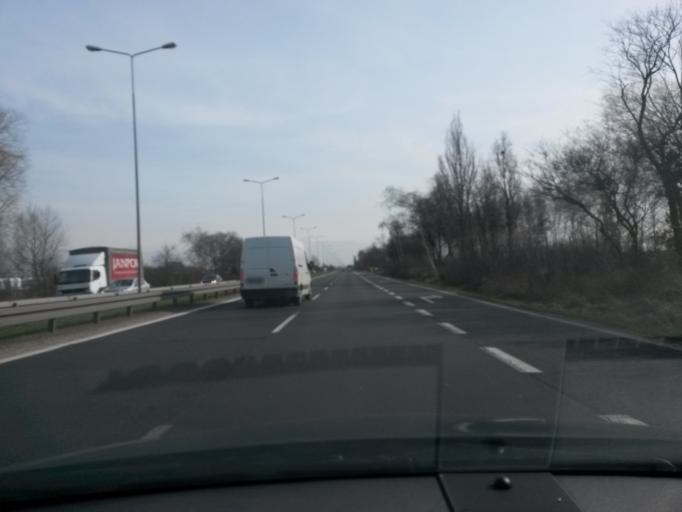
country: PL
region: Greater Poland Voivodeship
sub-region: Powiat poznanski
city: Daszewice
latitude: 52.3588
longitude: 16.9946
